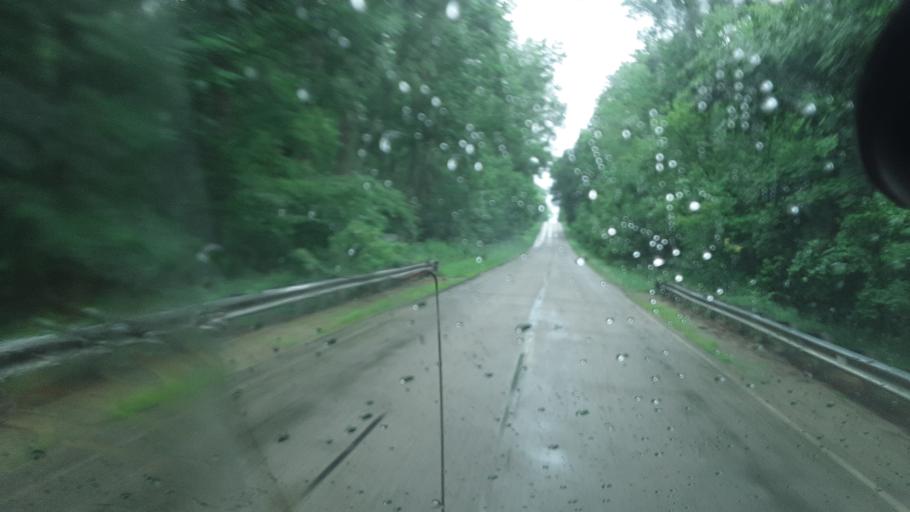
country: US
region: Ohio
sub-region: Williams County
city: Pioneer
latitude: 41.7085
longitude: -84.6921
